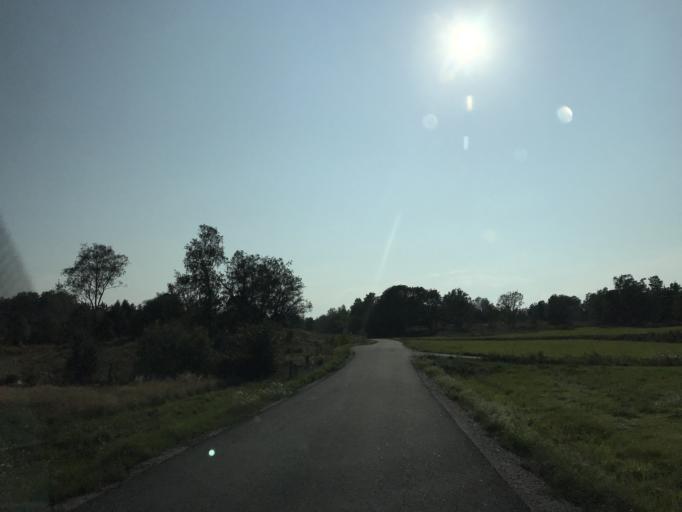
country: SE
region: Stockholm
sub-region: Norrtalje Kommun
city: Bjorko
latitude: 59.8536
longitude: 19.0160
